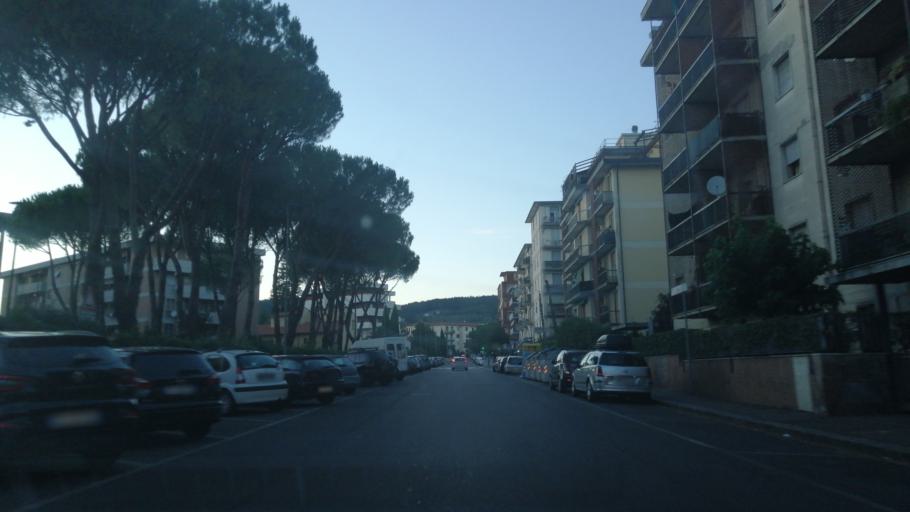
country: IT
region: Tuscany
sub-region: Province of Florence
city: Sesto Fiorentino
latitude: 43.8339
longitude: 11.2084
